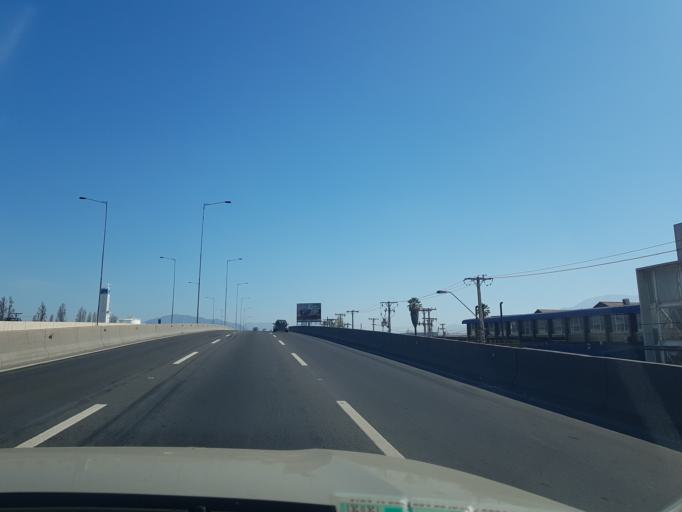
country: CL
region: Santiago Metropolitan
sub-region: Provincia de Santiago
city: Lo Prado
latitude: -33.3852
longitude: -70.7588
